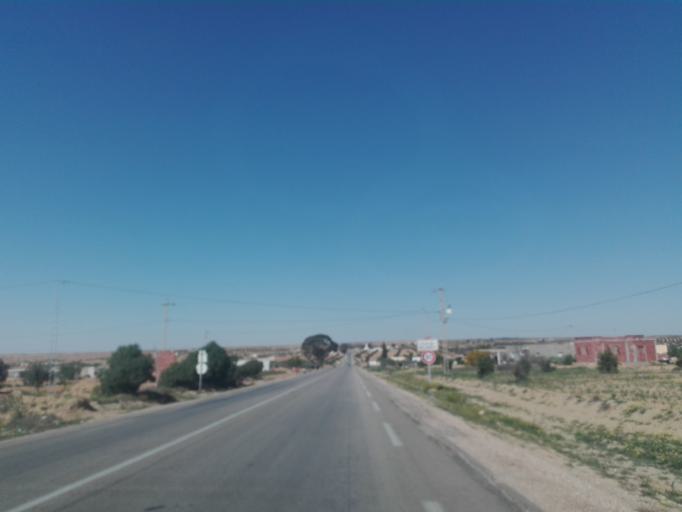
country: TN
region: Safaqis
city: Bi'r `Ali Bin Khalifah
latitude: 34.7410
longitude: 10.3850
